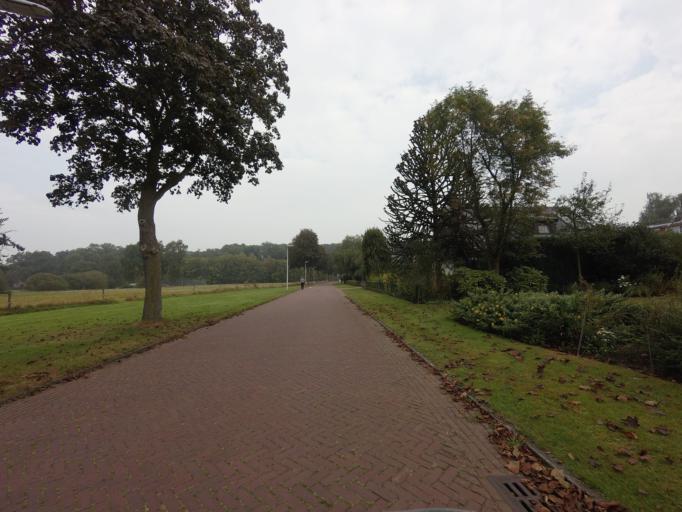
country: NL
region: Overijssel
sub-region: Gemeente Deventer
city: Schalkhaar
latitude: 52.2653
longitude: 6.1847
